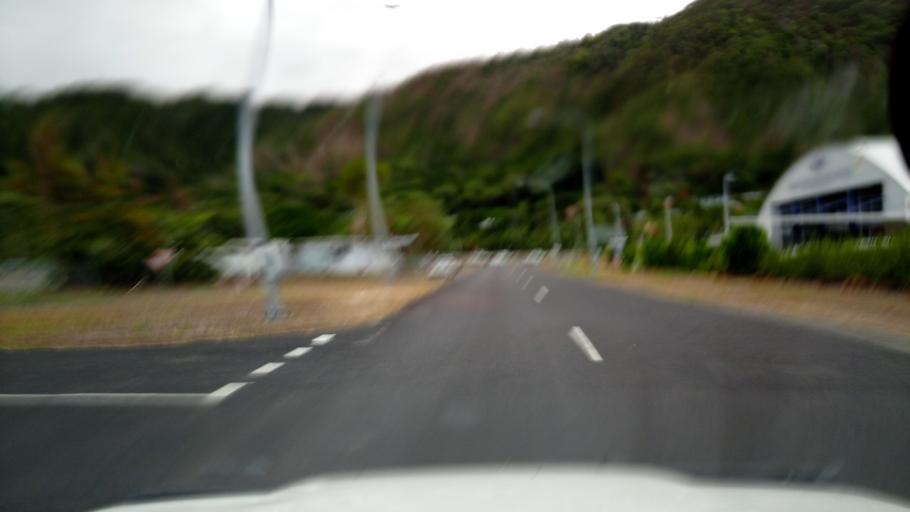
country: AU
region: Queensland
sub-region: Cairns
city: Cairns
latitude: -16.8823
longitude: 145.7479
